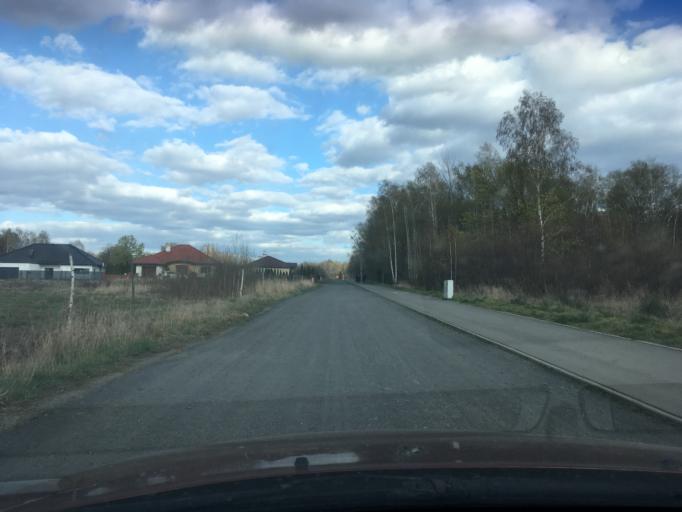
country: PL
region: Lower Silesian Voivodeship
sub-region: Powiat zgorzelecki
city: Zgorzelec
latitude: 51.1246
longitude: 15.0104
